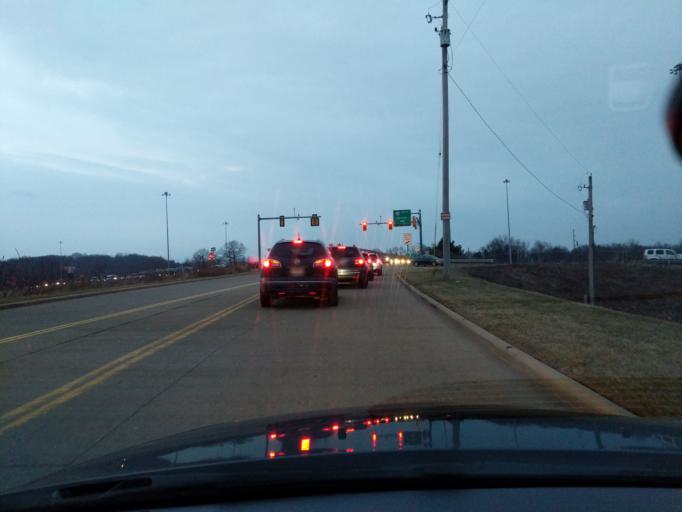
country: US
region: Ohio
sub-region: Summit County
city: Fairlawn
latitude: 41.0979
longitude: -81.5883
